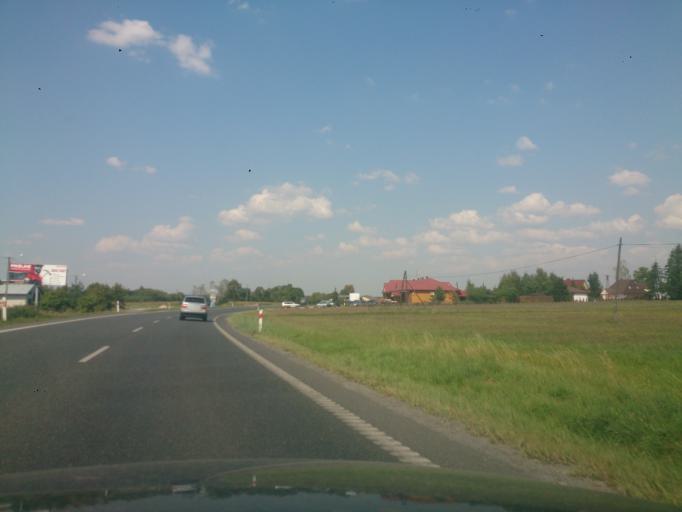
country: PL
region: Subcarpathian Voivodeship
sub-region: Powiat kolbuszowski
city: Kolbuszowa
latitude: 50.2632
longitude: 21.7591
